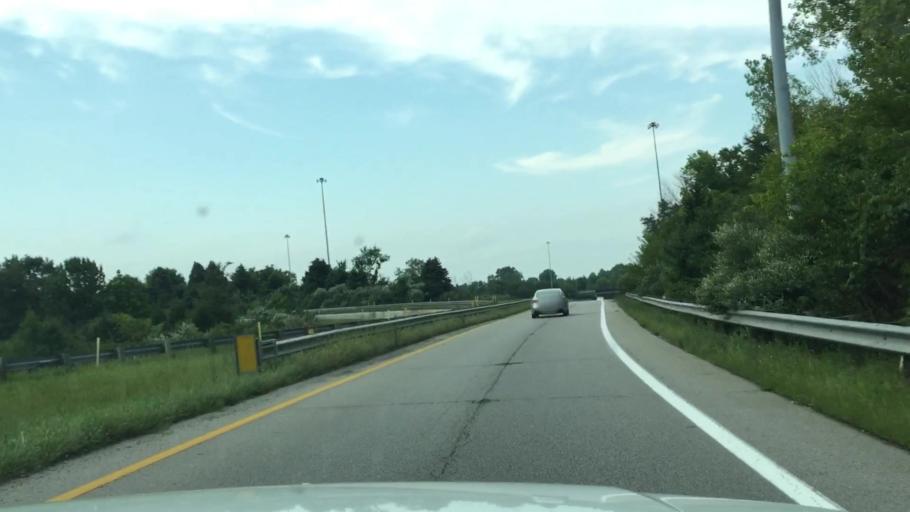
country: US
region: Ohio
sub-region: Franklin County
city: Groveport
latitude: 39.9016
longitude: -82.8959
